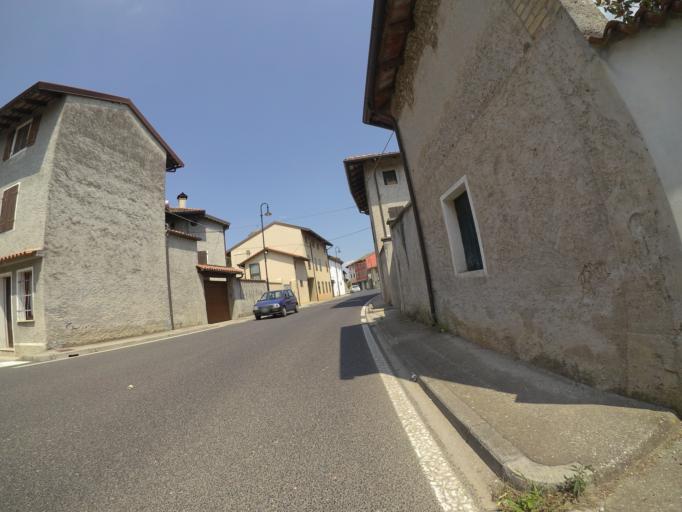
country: IT
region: Friuli Venezia Giulia
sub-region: Provincia di Udine
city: Codroipo
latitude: 45.9758
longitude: 12.9722
